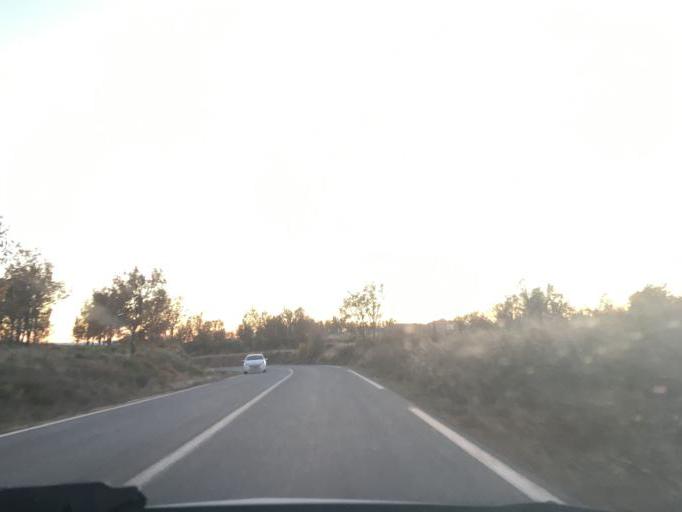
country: FR
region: Provence-Alpes-Cote d'Azur
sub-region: Departement du Var
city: Montferrat
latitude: 43.6480
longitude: 6.4743
